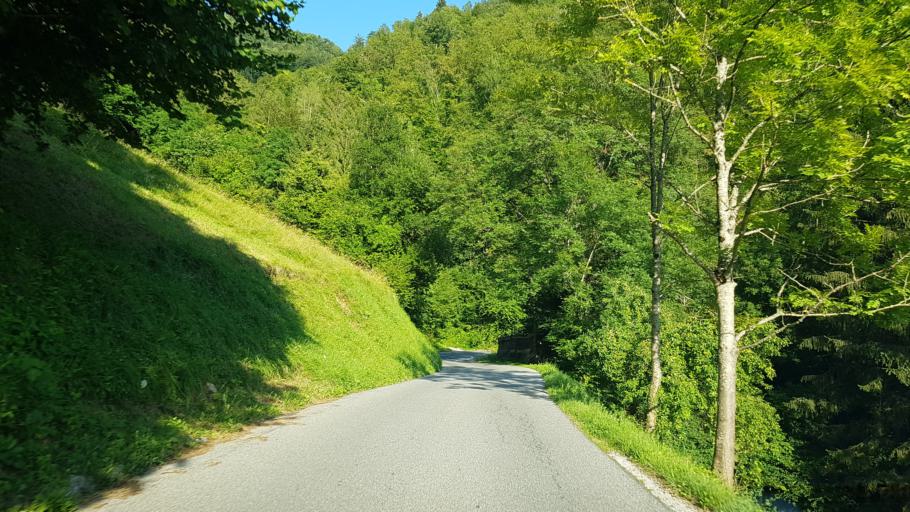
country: SI
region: Cerkno
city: Cerkno
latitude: 46.0859
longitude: 13.9846
